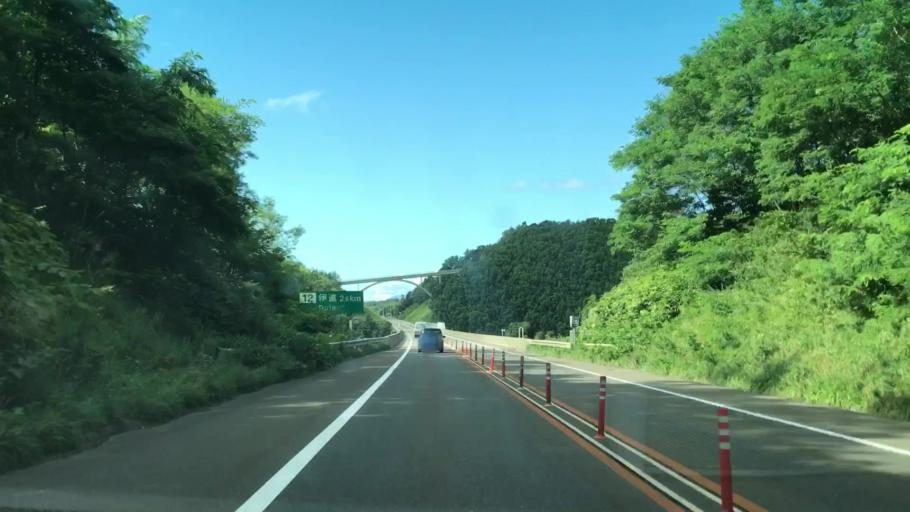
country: JP
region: Hokkaido
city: Date
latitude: 42.4577
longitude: 140.9122
